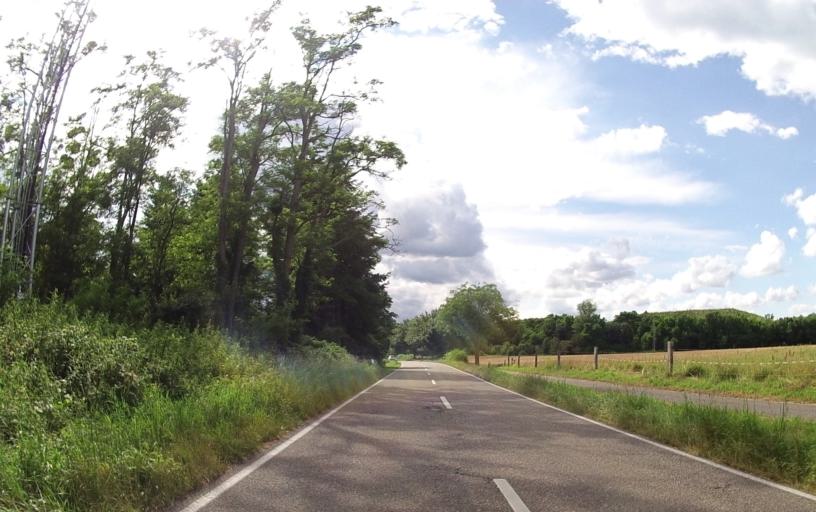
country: DE
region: Rheinland-Pfalz
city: Berg
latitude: 48.9785
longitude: 8.1793
